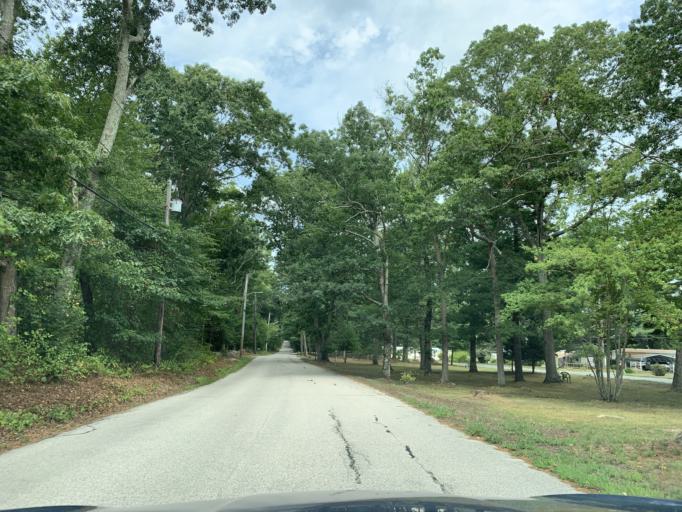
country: US
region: Rhode Island
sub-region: Washington County
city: Exeter
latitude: 41.5521
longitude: -71.6211
